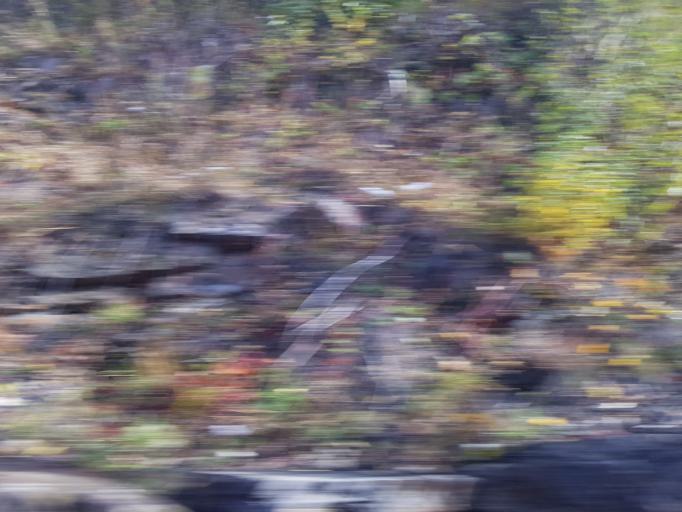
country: NO
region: Oppland
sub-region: Dovre
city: Dombas
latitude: 62.0414
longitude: 9.1490
